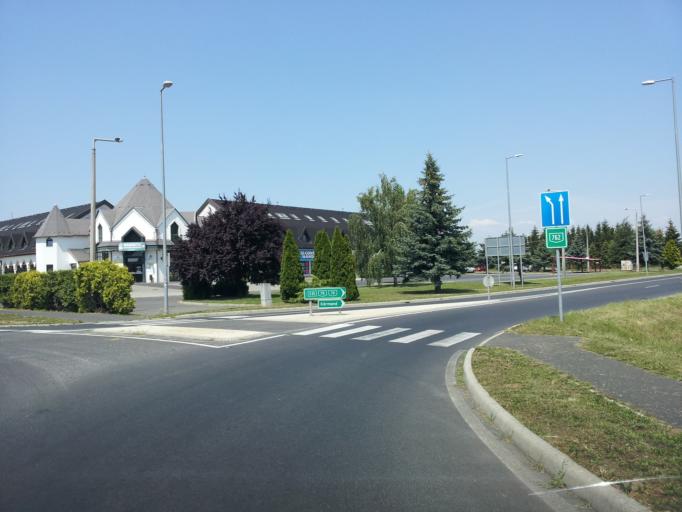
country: HU
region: Zala
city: Zalaegerszeg
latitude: 46.8684
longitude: 16.7946
